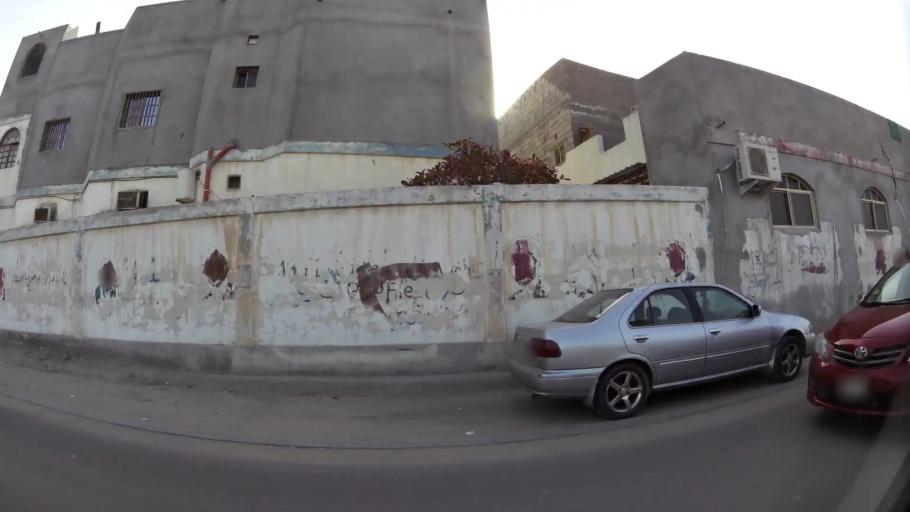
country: BH
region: Manama
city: Jidd Hafs
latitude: 26.2153
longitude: 50.5035
